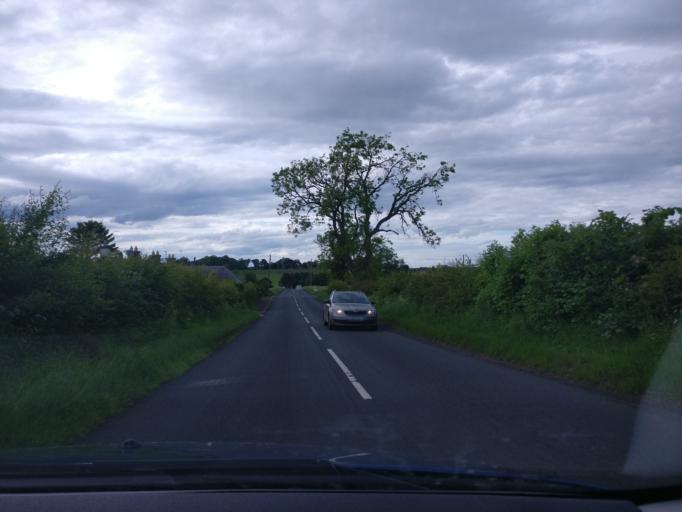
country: GB
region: Scotland
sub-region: East Lothian
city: Haddington
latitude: 55.9355
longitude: -2.7506
